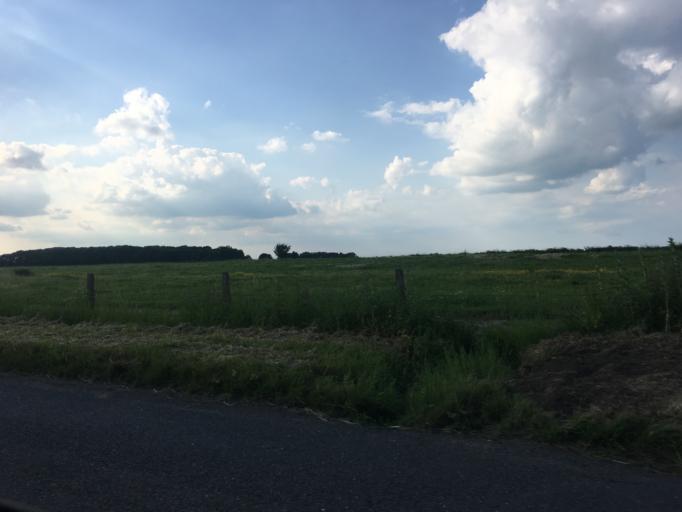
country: GB
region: England
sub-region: Leicestershire
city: Great Glen
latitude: 52.6095
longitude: -1.0304
